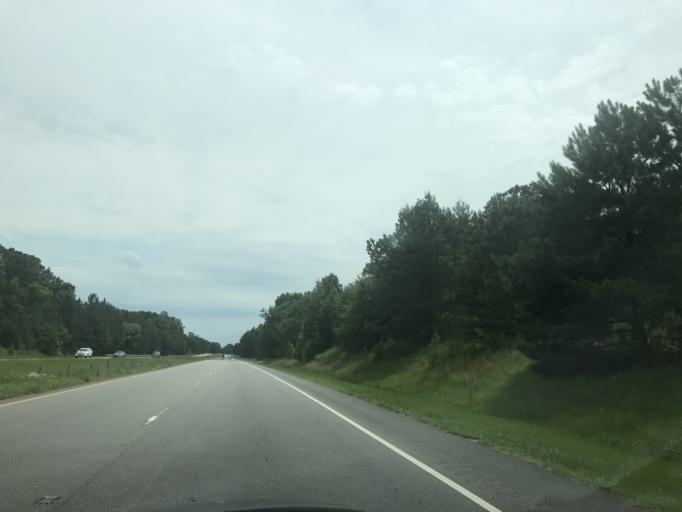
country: US
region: North Carolina
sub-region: Vance County
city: South Henderson
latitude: 36.2466
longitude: -78.4341
